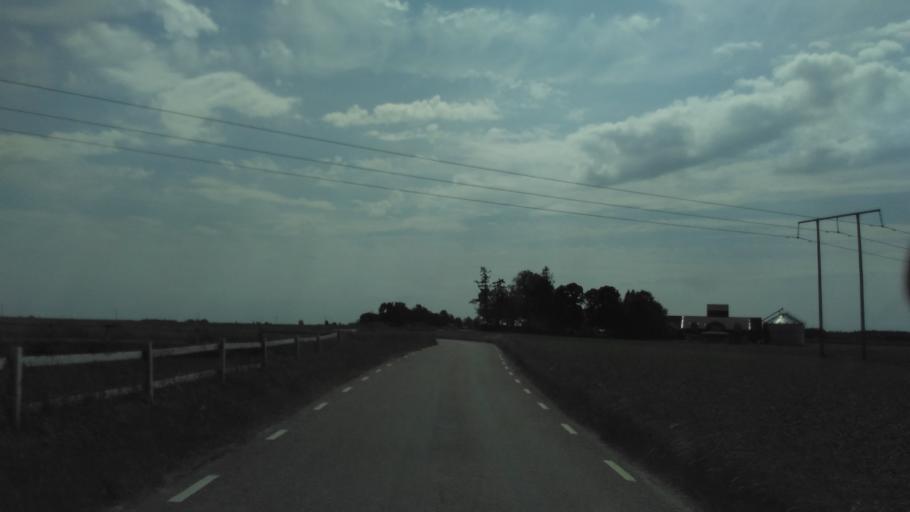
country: SE
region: Vaestra Goetaland
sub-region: Grastorps Kommun
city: Graestorp
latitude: 58.3875
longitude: 12.7894
